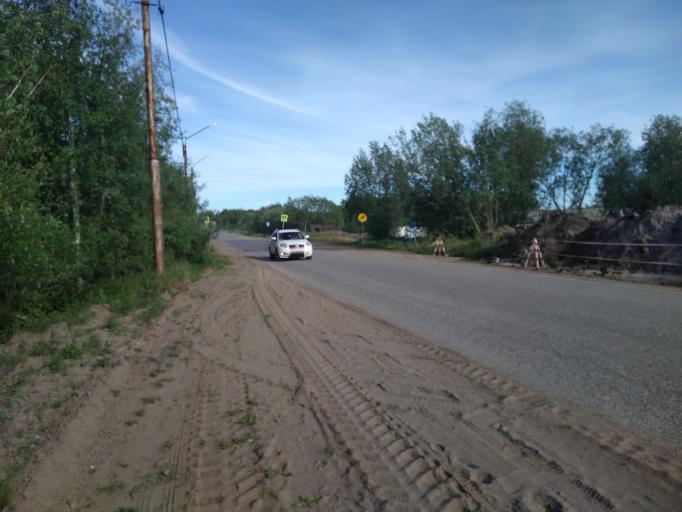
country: RU
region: Komi Republic
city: Pechora
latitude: 65.1417
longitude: 57.2529
